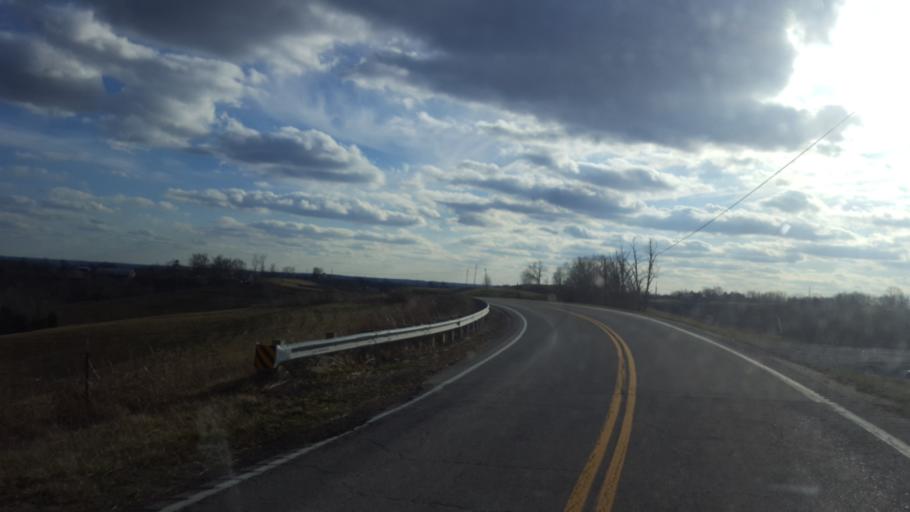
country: US
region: Kentucky
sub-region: Robertson County
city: Mount Olivet
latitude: 38.5005
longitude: -84.0483
